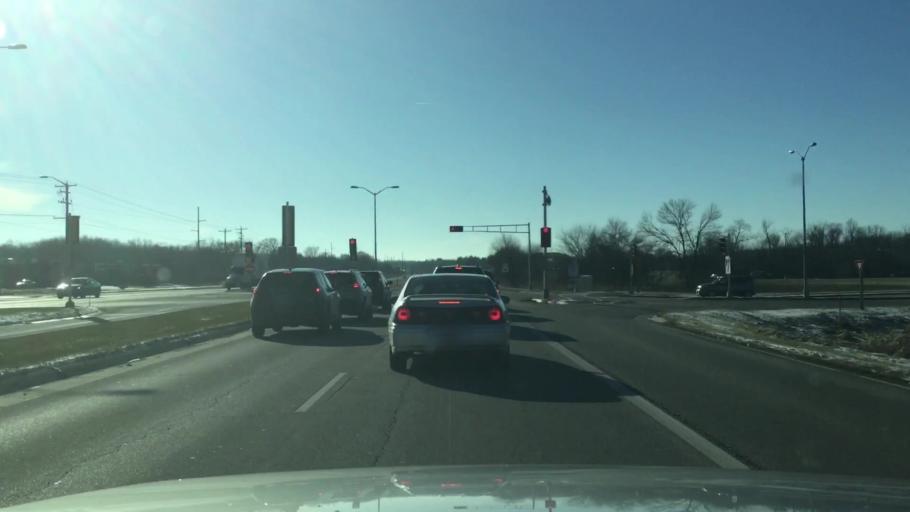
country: US
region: Wisconsin
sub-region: Racine County
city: Browns Lake
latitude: 42.7047
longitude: -88.2477
